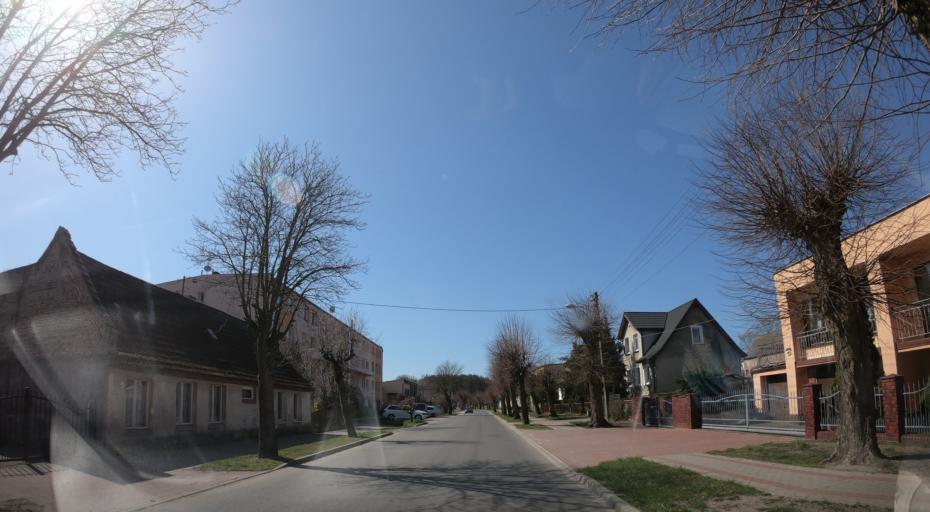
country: PL
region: West Pomeranian Voivodeship
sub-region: Powiat kamienski
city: Wolin
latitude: 53.8377
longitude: 14.6102
